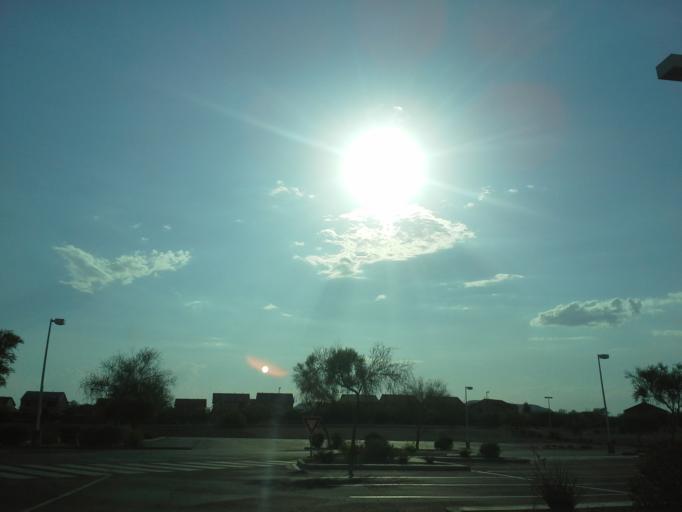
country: US
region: Arizona
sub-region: Maricopa County
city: Anthem
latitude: 33.8747
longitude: -112.1503
